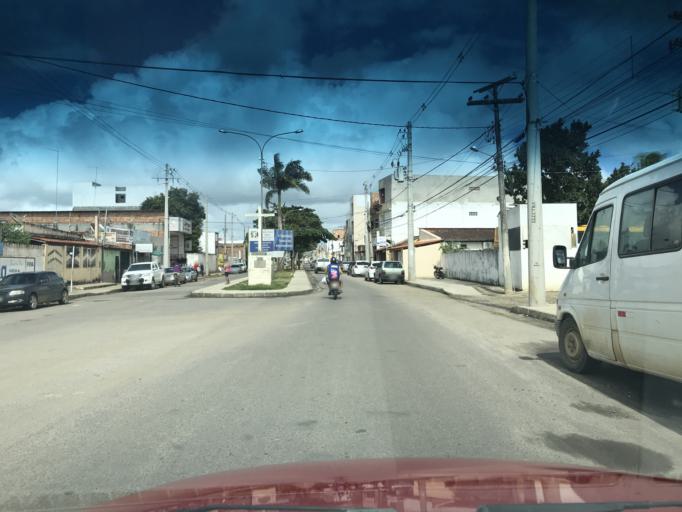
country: BR
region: Bahia
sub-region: Santo Antonio De Jesus
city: Santo Antonio de Jesus
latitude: -12.9684
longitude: -39.2708
